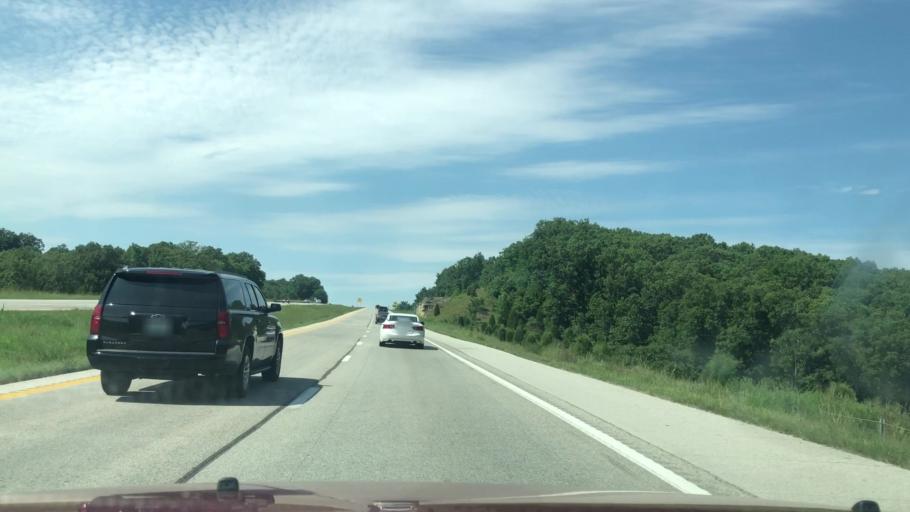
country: US
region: Missouri
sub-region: Taney County
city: Merriam Woods
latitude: 36.8362
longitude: -93.2186
